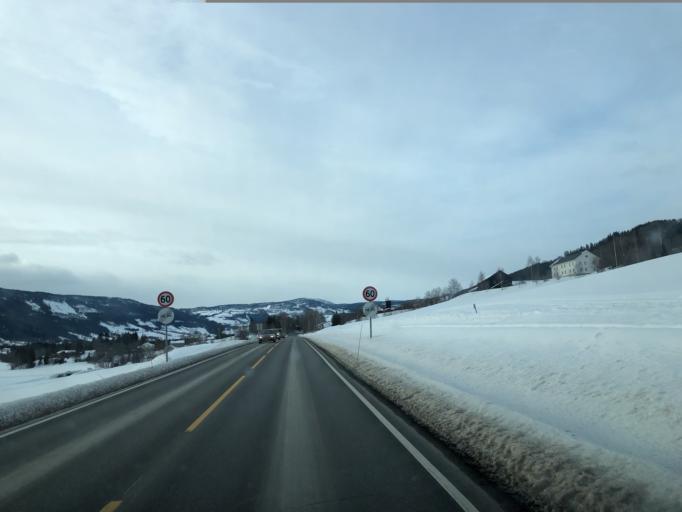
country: NO
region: Oppland
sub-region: Gausdal
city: Segalstad bru
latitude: 61.2356
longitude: 10.2080
